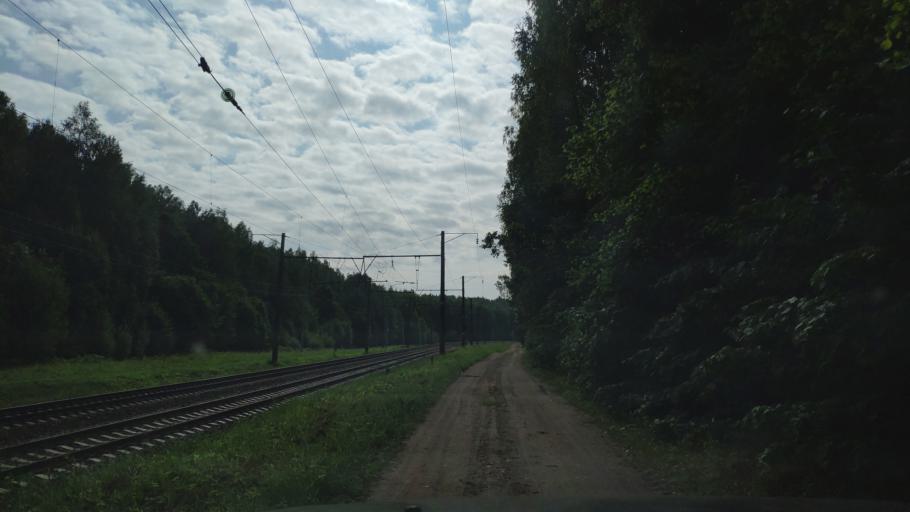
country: BY
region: Minsk
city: Khatsyezhyna
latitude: 53.9618
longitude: 27.3037
